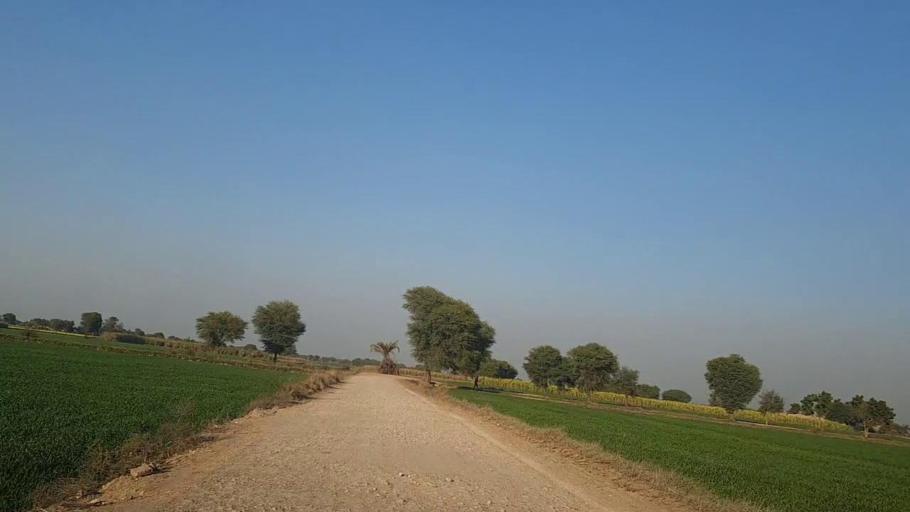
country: PK
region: Sindh
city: Sakrand
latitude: 26.2976
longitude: 68.1234
